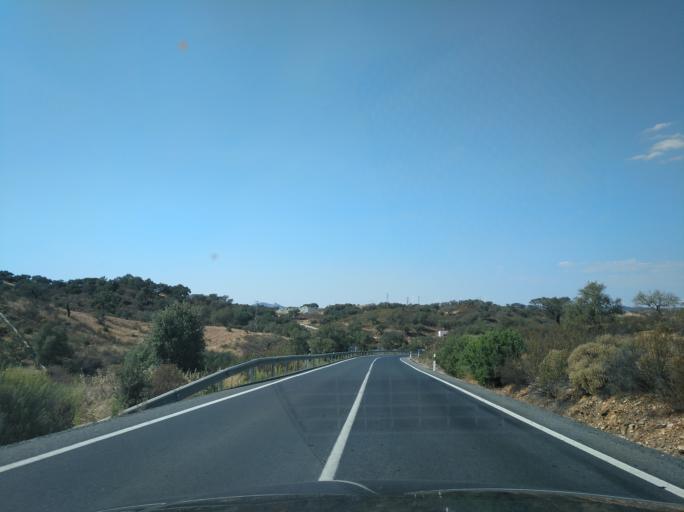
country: ES
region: Andalusia
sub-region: Provincia de Huelva
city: Alosno
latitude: 37.5216
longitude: -7.1351
